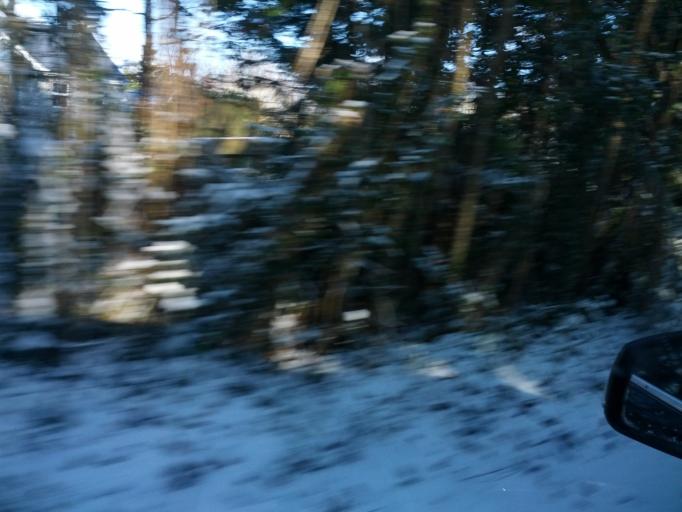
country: IE
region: Connaught
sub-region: County Galway
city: Gort
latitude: 53.1841
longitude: -8.8135
